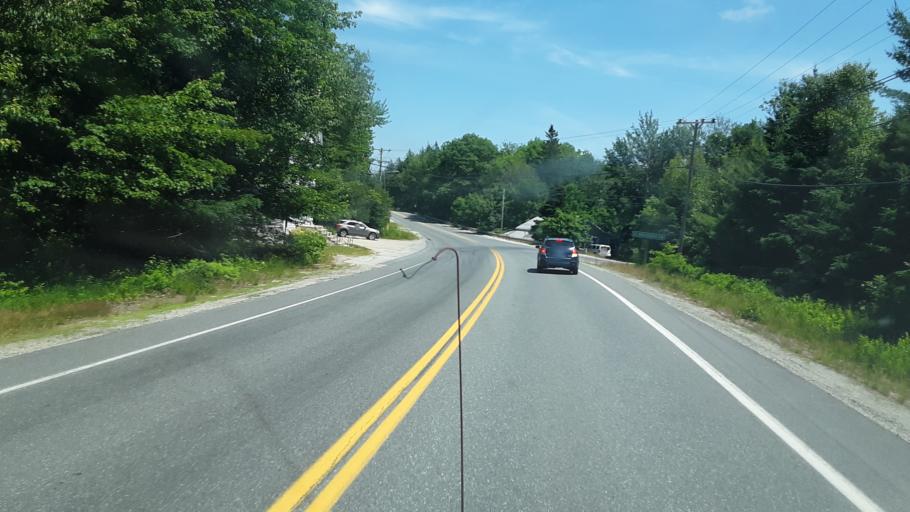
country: US
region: Maine
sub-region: Hancock County
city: Gouldsboro
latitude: 44.4704
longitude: -68.0918
